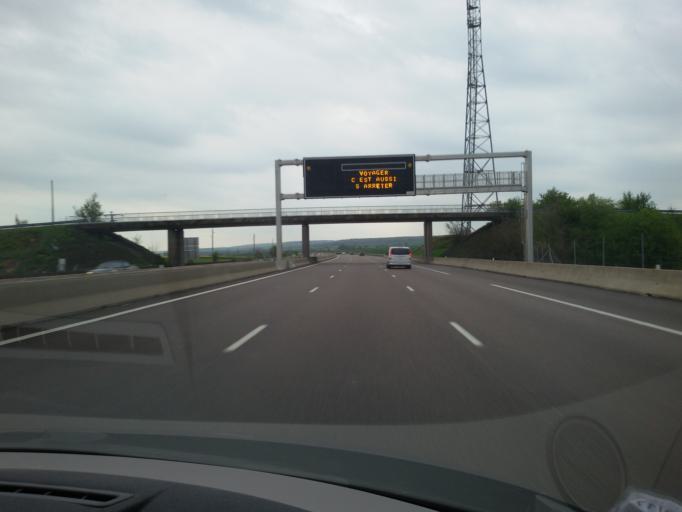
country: FR
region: Champagne-Ardenne
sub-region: Departement de la Haute-Marne
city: Rolampont
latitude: 47.8864
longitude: 5.2229
